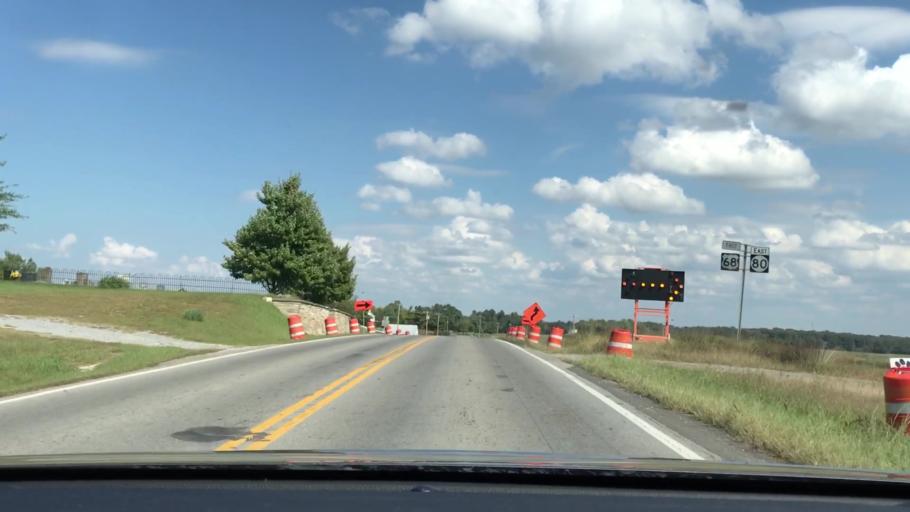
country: US
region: Kentucky
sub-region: Trigg County
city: Cadiz
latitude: 36.8202
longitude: -87.8741
